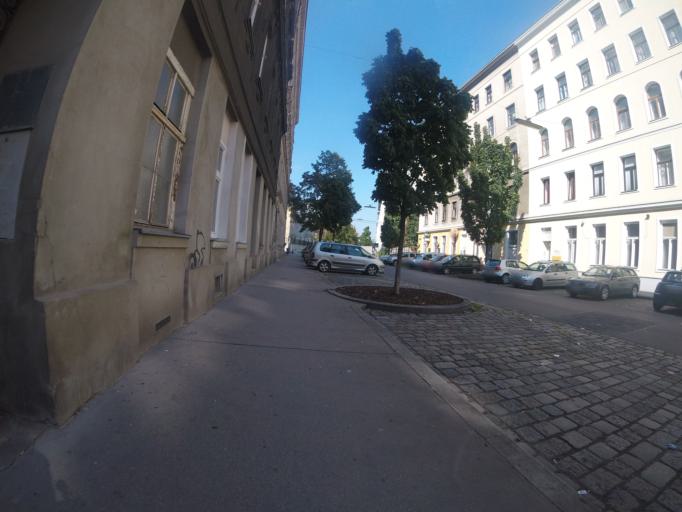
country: AT
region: Lower Austria
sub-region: Politischer Bezirk Wien-Umgebung
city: Leopoldsdorf
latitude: 48.1438
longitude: 16.4160
